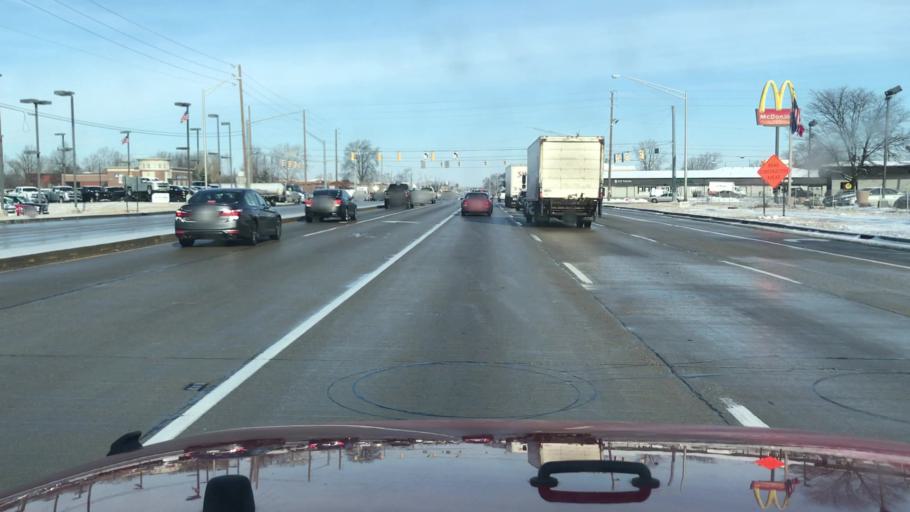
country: US
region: Indiana
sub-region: Boone County
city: Zionsville
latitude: 39.9251
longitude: -86.2290
